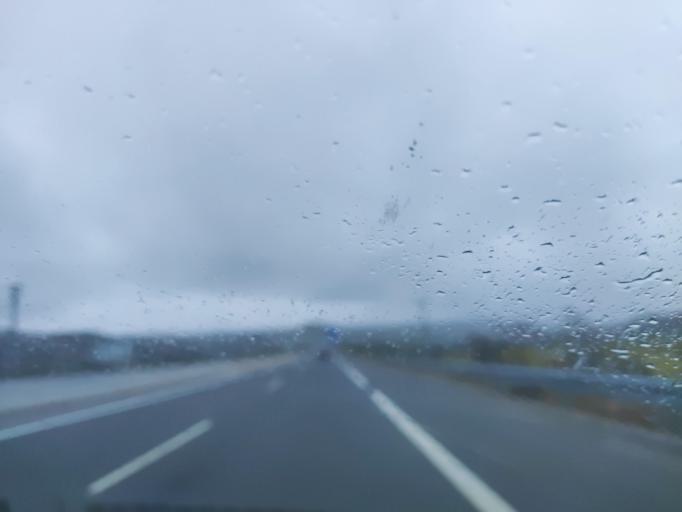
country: ES
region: Castille-La Mancha
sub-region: Province of Toledo
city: Toledo
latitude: 39.8700
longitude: -4.0819
